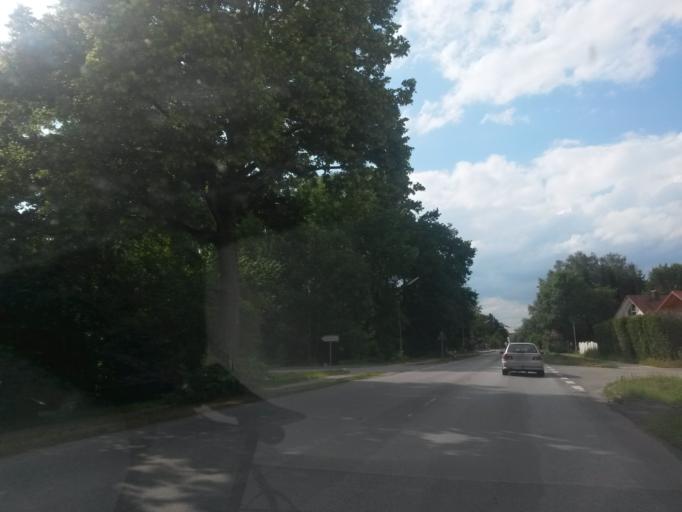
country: DE
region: Bavaria
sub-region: Upper Bavaria
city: Fahrenzhausen
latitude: 48.3443
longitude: 11.5693
